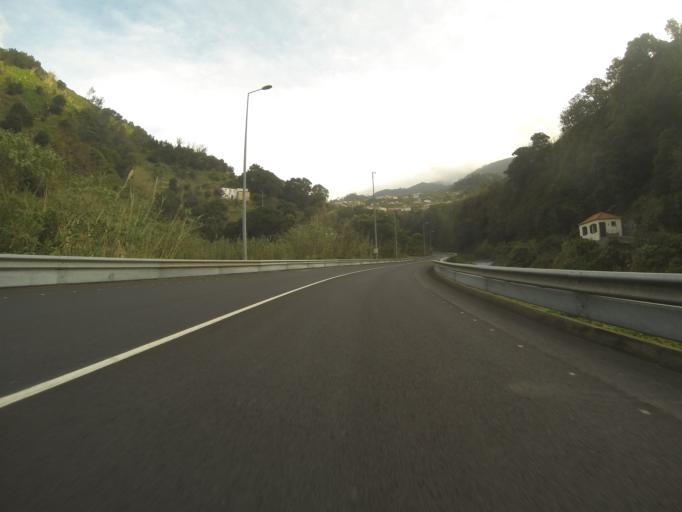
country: PT
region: Madeira
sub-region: Sao Vicente
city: Sao Vicente
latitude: 32.7968
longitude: -17.0403
